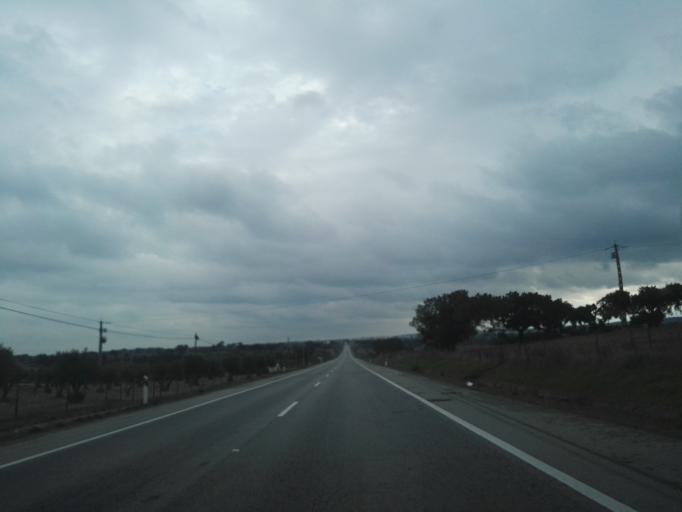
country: PT
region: Portalegre
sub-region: Arronches
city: Arronches
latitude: 39.1431
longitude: -7.3013
